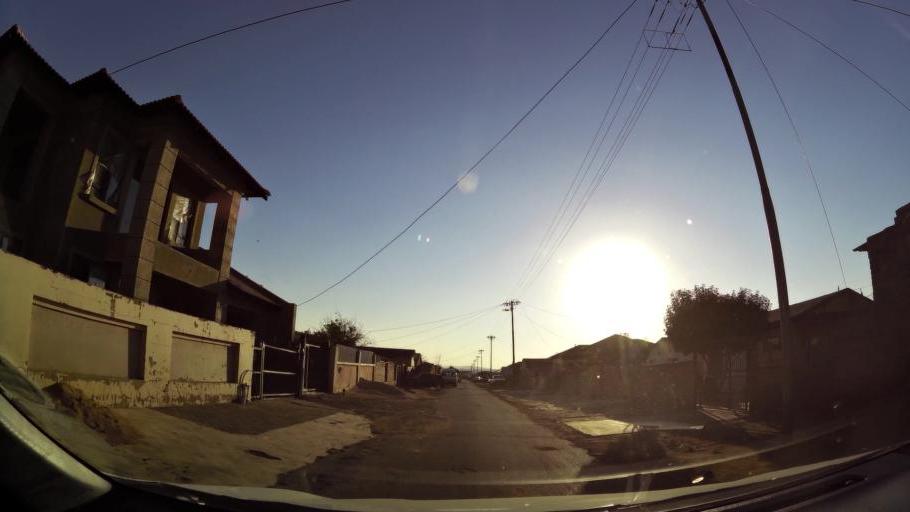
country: ZA
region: Gauteng
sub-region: City of Tshwane Metropolitan Municipality
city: Cullinan
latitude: -25.7230
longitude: 28.3900
